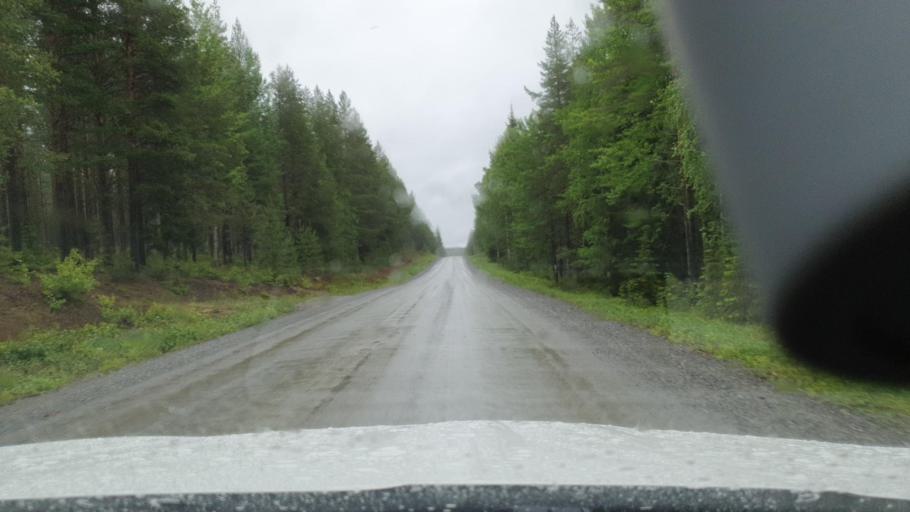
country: SE
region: Vaesterbotten
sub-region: Skelleftea Kommun
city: Burtraesk
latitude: 64.3817
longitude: 20.3290
